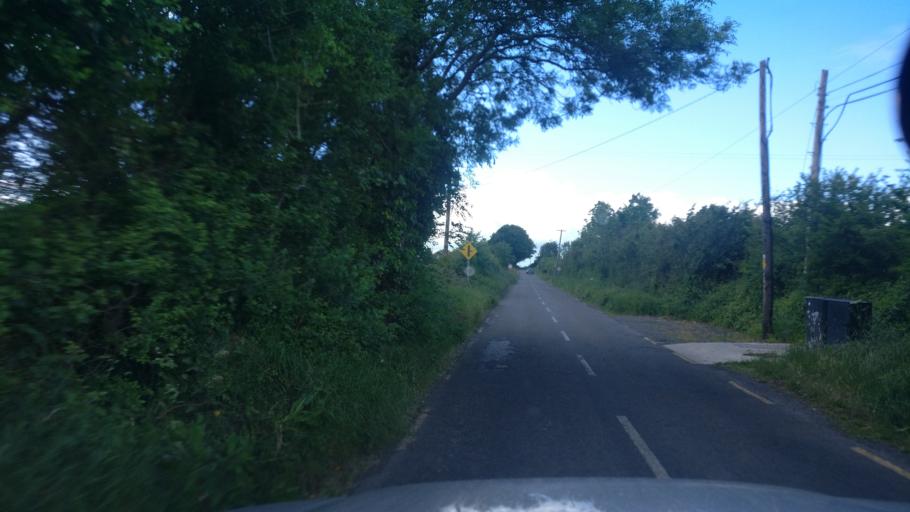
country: IE
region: Connaught
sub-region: County Galway
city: Portumna
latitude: 53.1751
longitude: -8.2924
